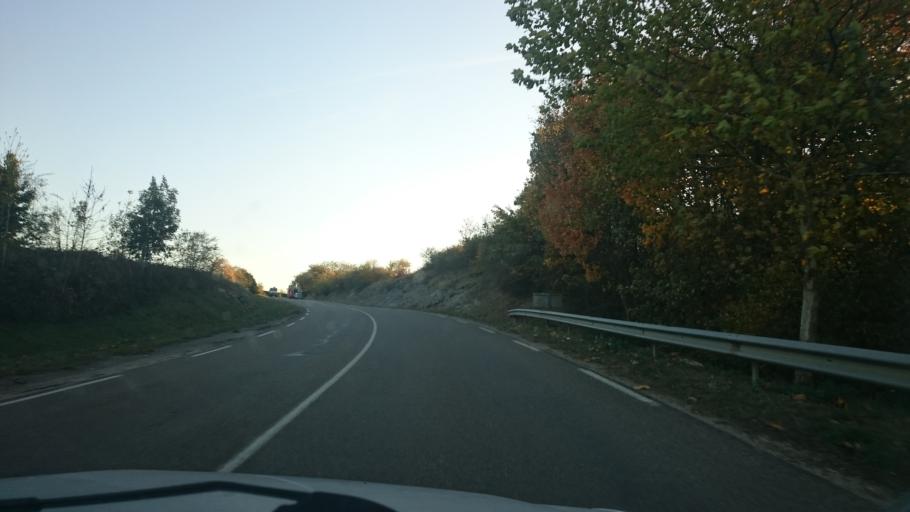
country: FR
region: Franche-Comte
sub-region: Departement du Doubs
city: Quingey
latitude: 47.0862
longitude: 5.8833
